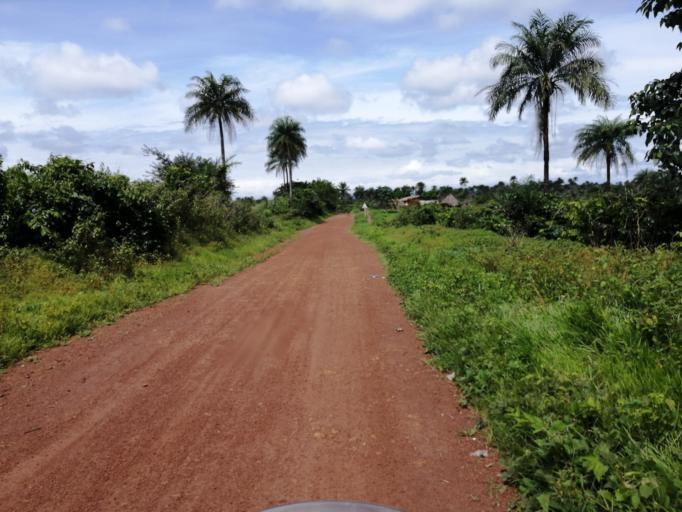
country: SL
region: Northern Province
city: Pepel
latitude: 8.6533
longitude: -13.0077
